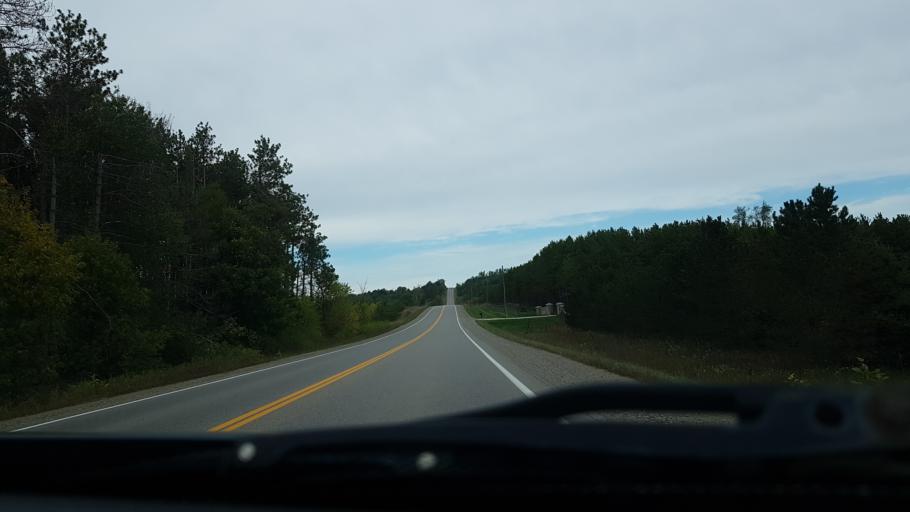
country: CA
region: Ontario
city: Shelburne
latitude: 44.0839
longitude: -80.0195
